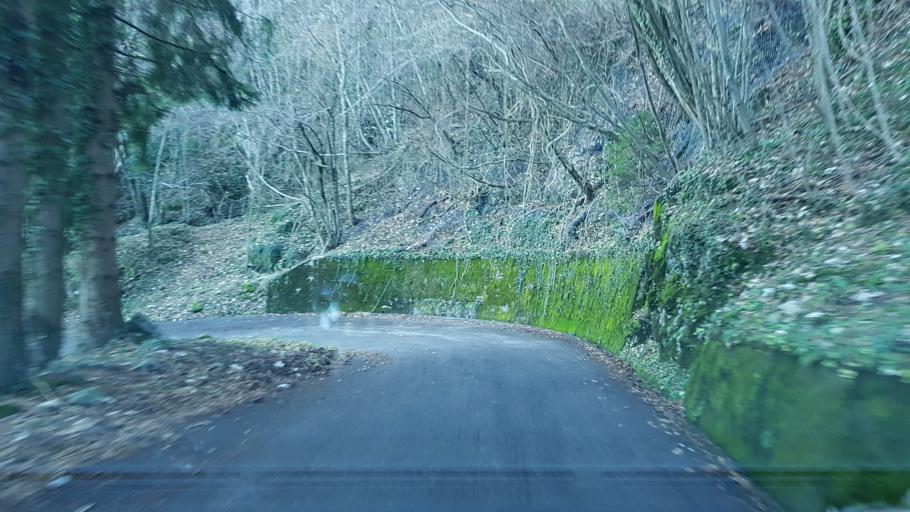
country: IT
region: Friuli Venezia Giulia
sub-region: Provincia di Udine
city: Savogna
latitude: 46.1837
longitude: 13.5331
